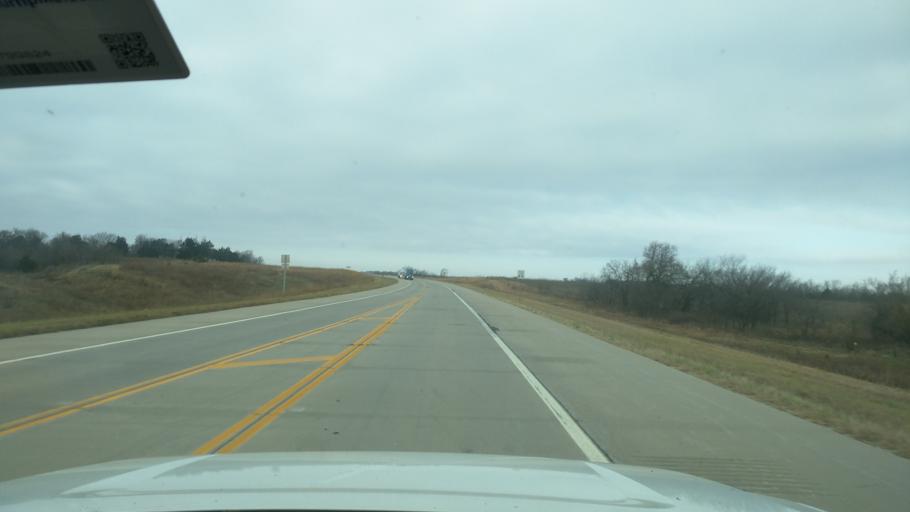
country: US
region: Kansas
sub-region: Elk County
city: Howard
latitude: 37.6371
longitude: -96.2368
